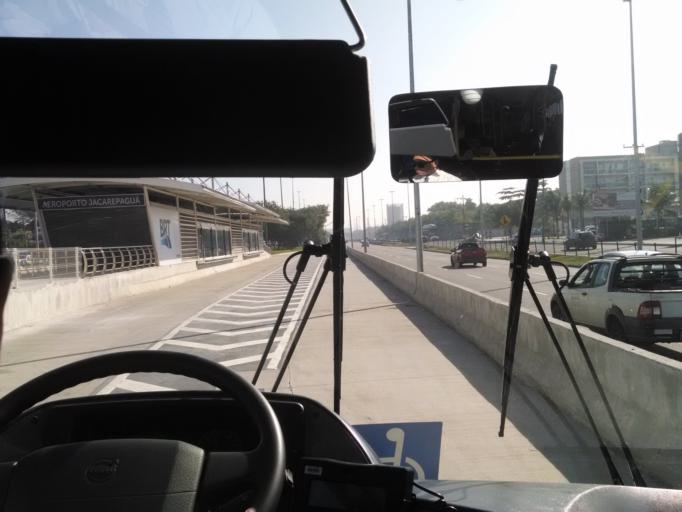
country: BR
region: Rio de Janeiro
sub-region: Rio De Janeiro
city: Rio de Janeiro
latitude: -22.9896
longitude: -43.3657
